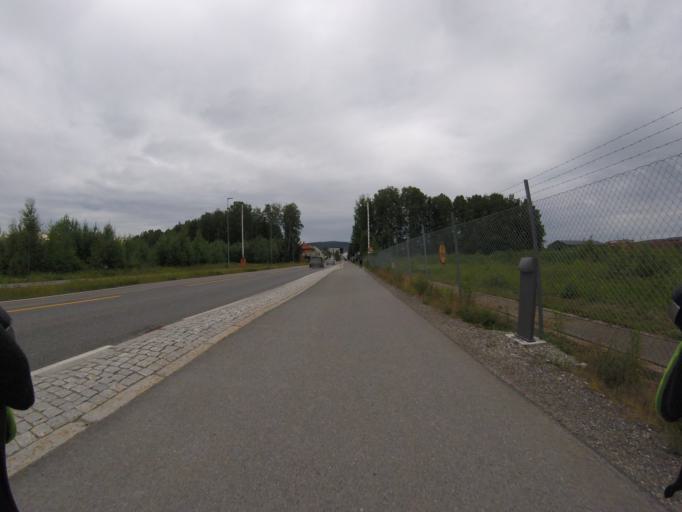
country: NO
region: Akershus
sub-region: Skedsmo
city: Lillestrom
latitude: 59.9648
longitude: 11.0517
